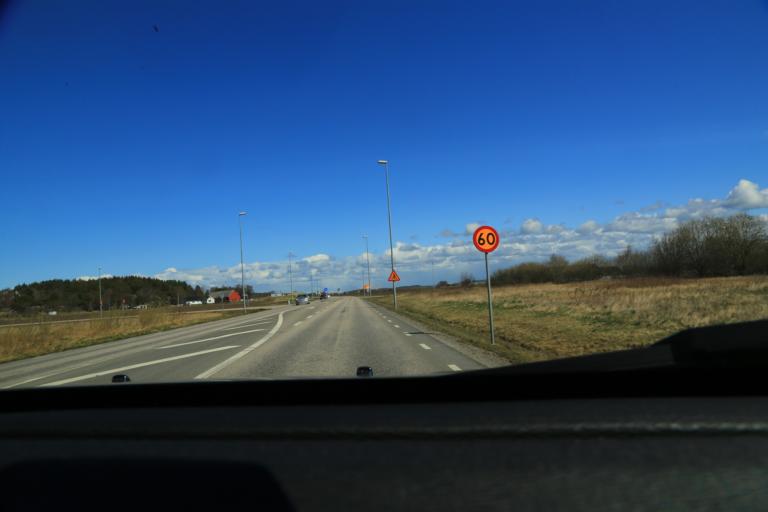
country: SE
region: Halland
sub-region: Varbergs Kommun
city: Traslovslage
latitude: 57.0879
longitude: 12.2879
